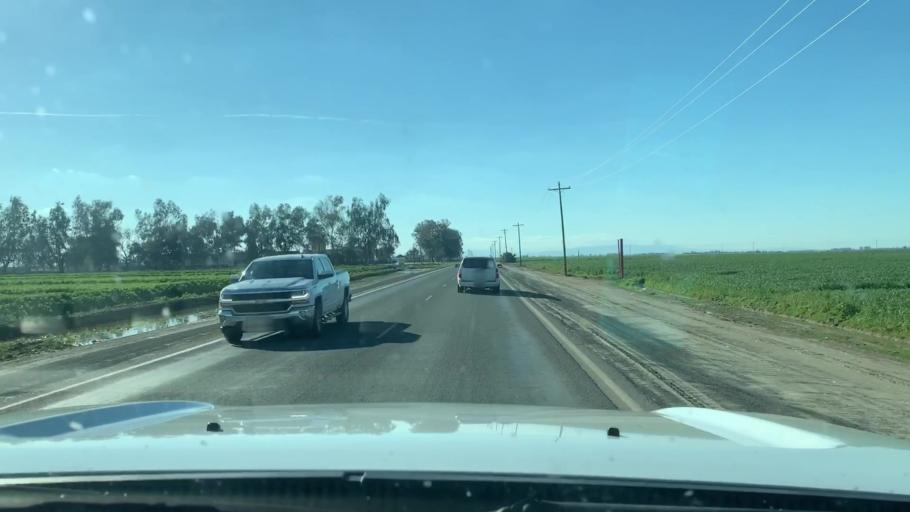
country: US
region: California
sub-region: Kings County
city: Armona
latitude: 36.2111
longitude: -119.7013
